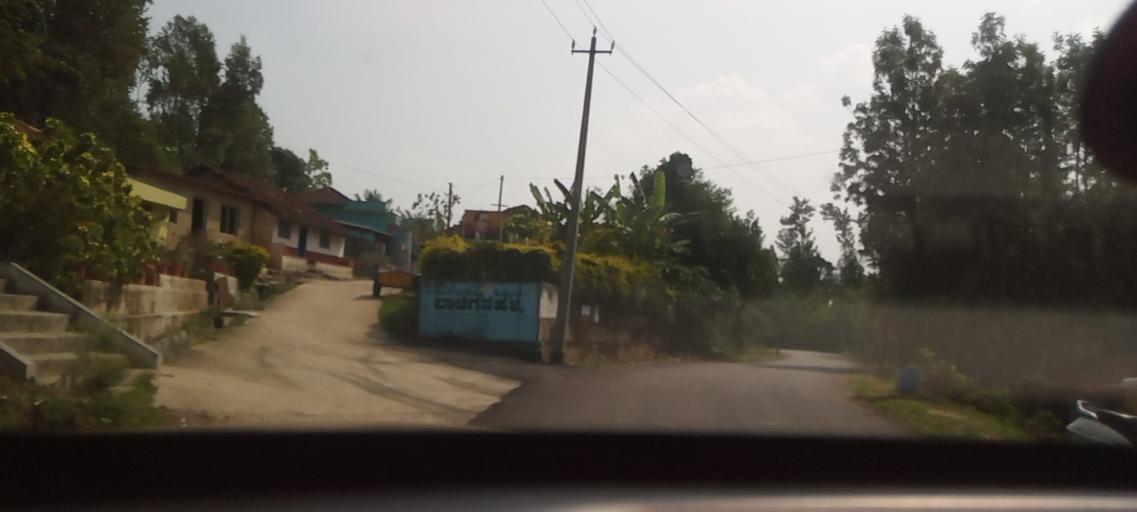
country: IN
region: Karnataka
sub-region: Chikmagalur
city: Chikmagalur
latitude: 13.2676
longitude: 75.7226
